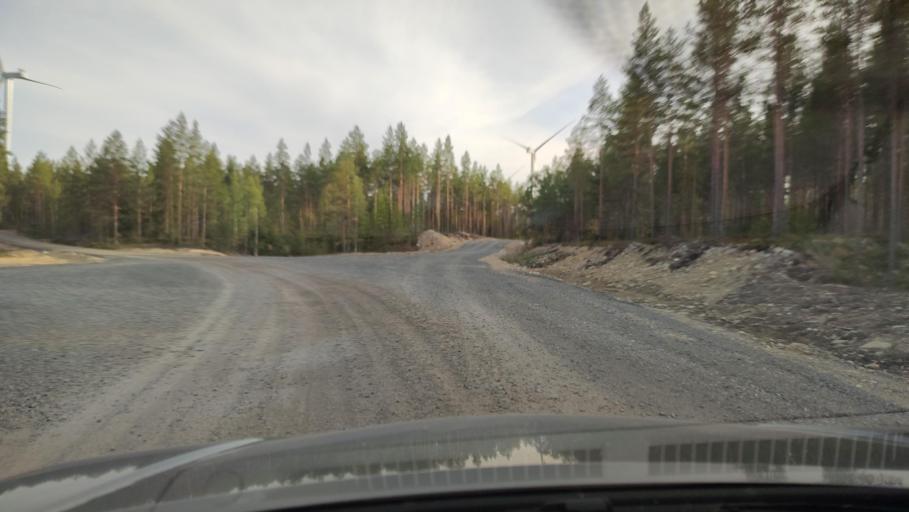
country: FI
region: Southern Ostrobothnia
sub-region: Suupohja
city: Karijoki
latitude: 62.1585
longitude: 21.6123
